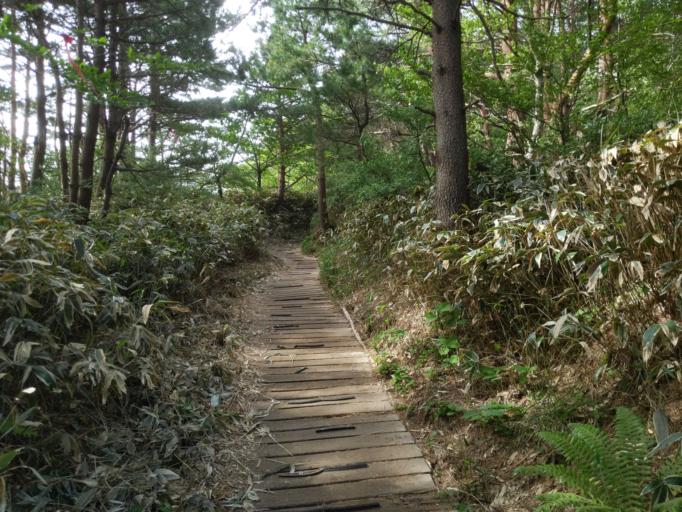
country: KR
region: Jeju-do
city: Jeju-si
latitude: 33.3814
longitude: 126.5340
